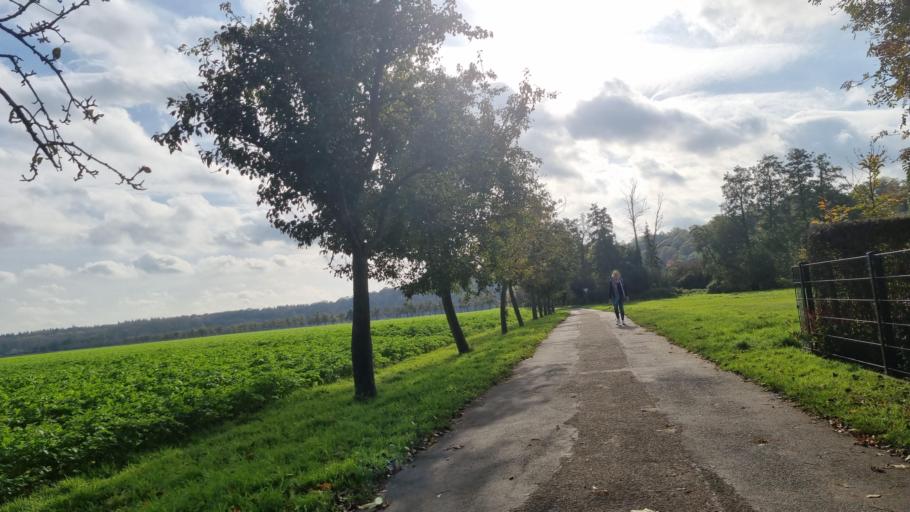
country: DE
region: North Rhine-Westphalia
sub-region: Regierungsbezirk Dusseldorf
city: Kleve
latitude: 51.7813
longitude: 6.1421
